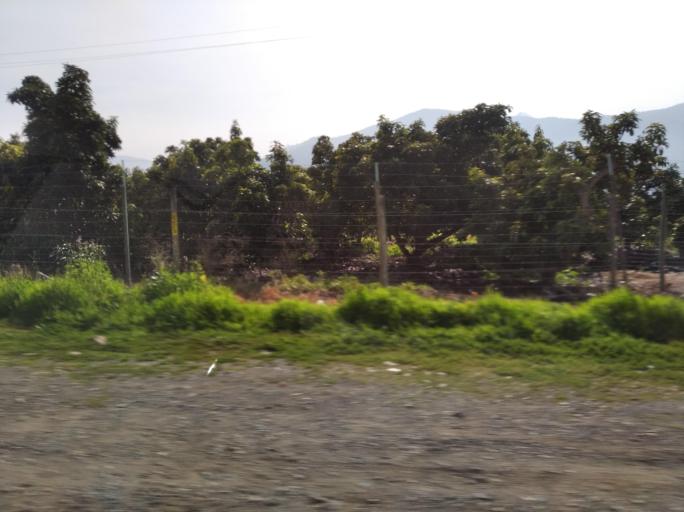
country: CL
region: Valparaiso
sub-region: Provincia de Marga Marga
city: Limache
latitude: -33.0245
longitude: -71.1578
